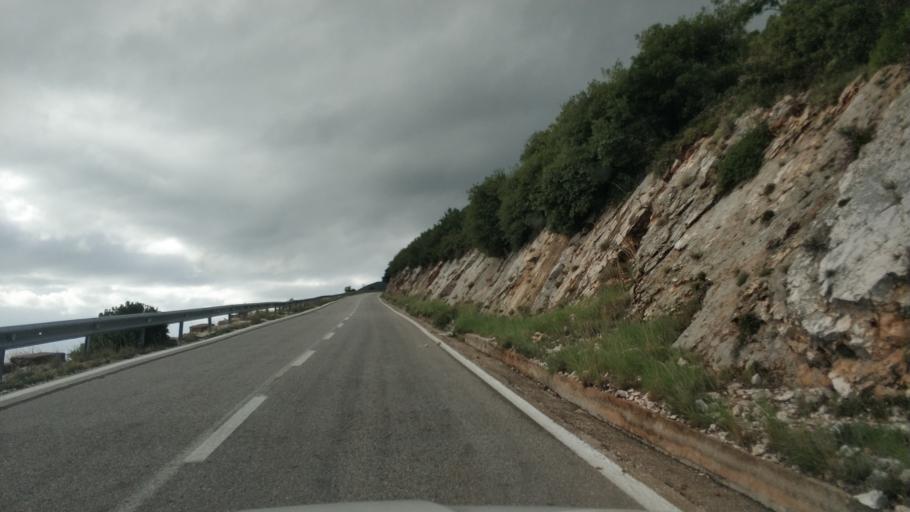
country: AL
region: Vlore
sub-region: Rrethi i Vlores
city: Vranisht
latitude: 40.1778
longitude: 19.6021
